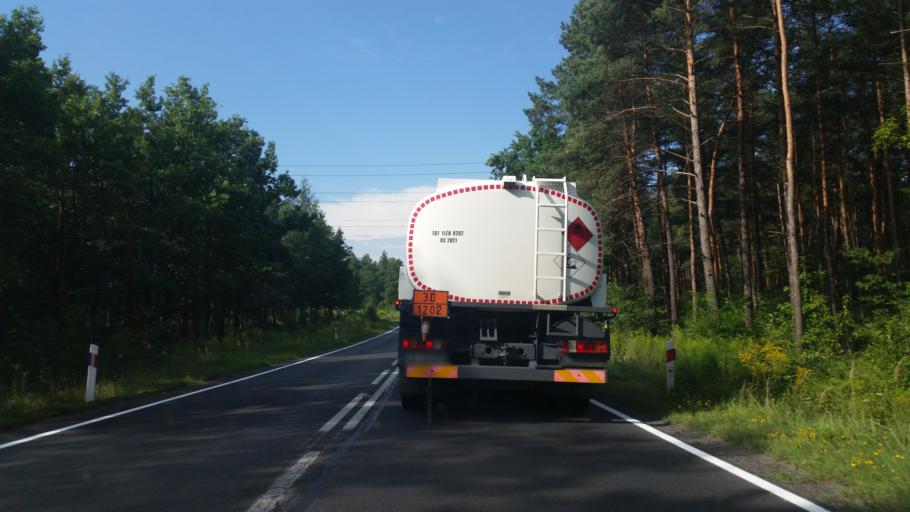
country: PL
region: Lesser Poland Voivodeship
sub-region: Powiat chrzanowski
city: Zarki
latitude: 50.1191
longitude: 19.3598
